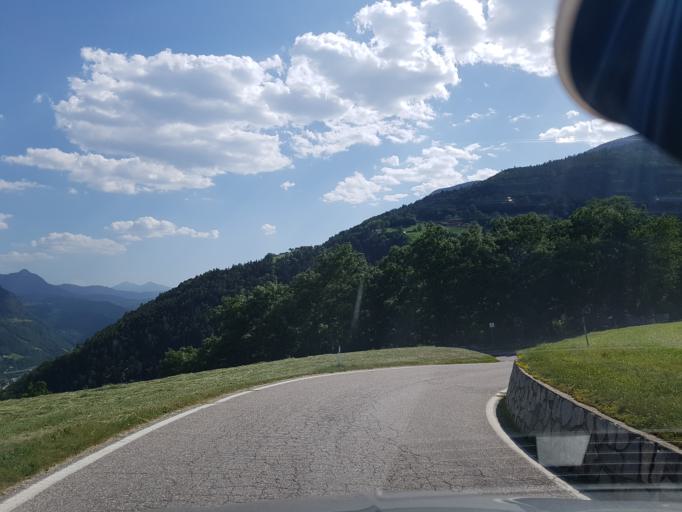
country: IT
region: Trentino-Alto Adige
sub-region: Bolzano
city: Villandro - Villanders
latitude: 46.6215
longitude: 11.5316
